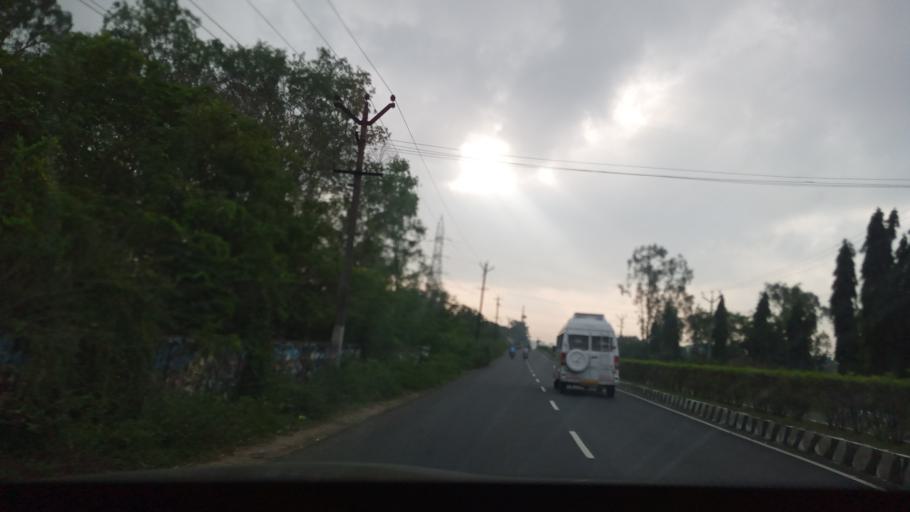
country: IN
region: Tamil Nadu
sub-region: Kancheepuram
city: Vengavasal
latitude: 12.8077
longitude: 80.1876
